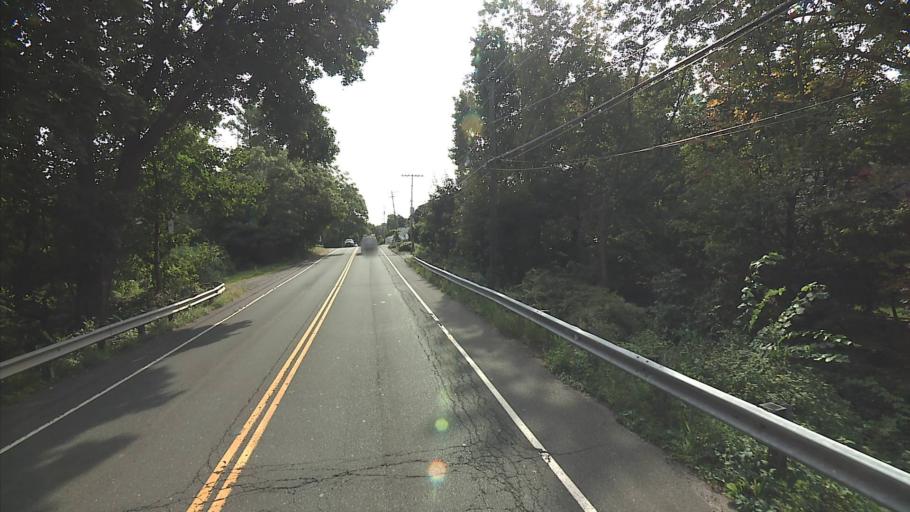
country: US
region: Connecticut
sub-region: Fairfield County
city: New Canaan
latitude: 41.1509
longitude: -73.4883
